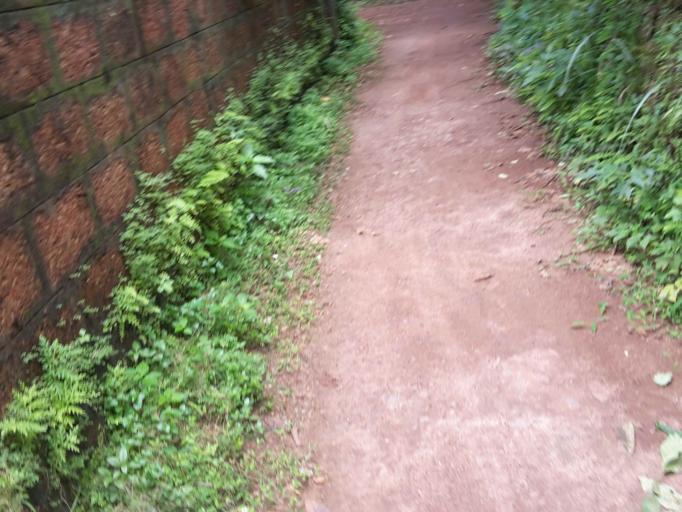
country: IN
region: Kerala
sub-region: Kozhikode
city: Kozhikode
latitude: 11.2835
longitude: 75.7952
